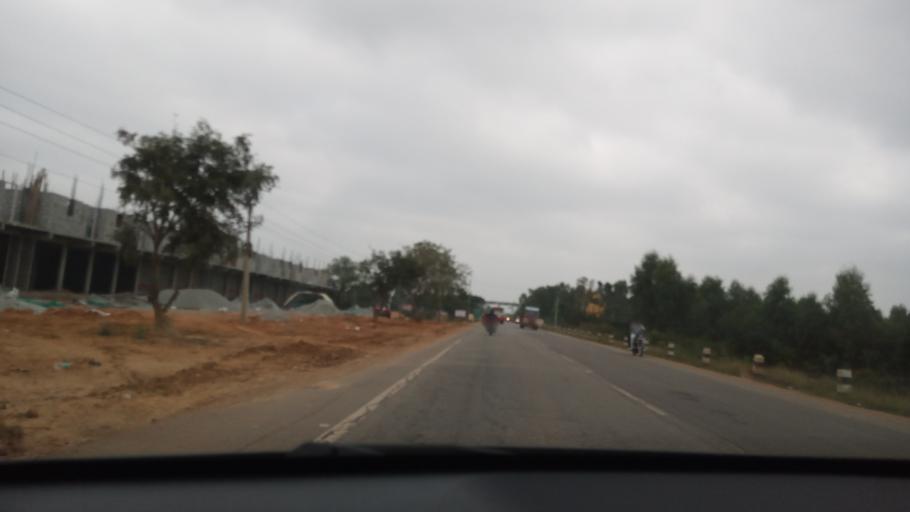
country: IN
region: Karnataka
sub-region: Bangalore Rural
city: Vijayapura
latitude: 13.2579
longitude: 77.9418
